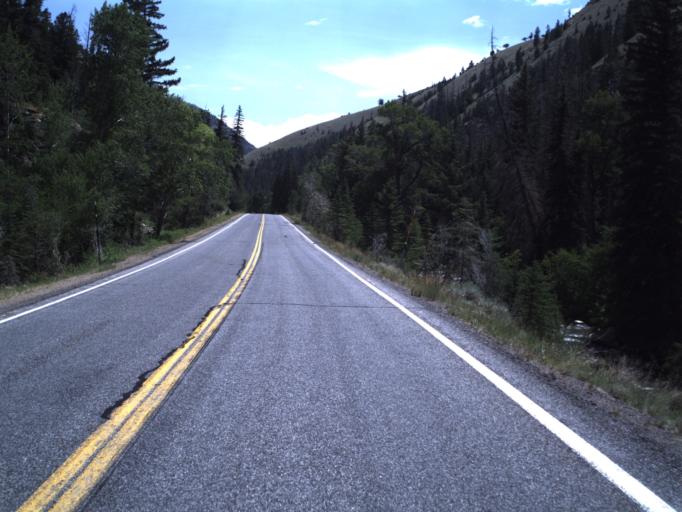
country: US
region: Utah
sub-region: Emery County
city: Huntington
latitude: 39.4726
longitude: -111.1558
